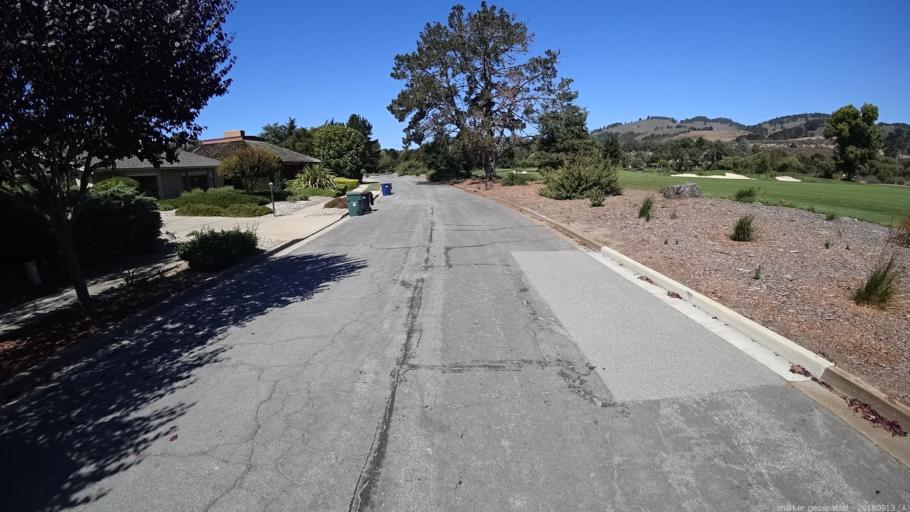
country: US
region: California
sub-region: Monterey County
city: Del Rey Oaks
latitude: 36.5294
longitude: -121.8557
